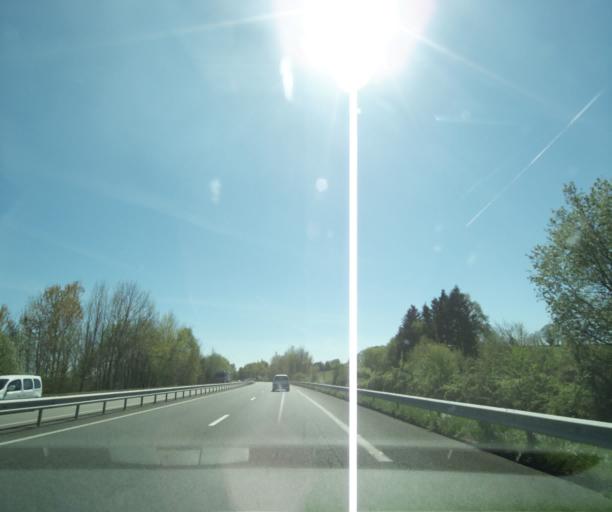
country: FR
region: Limousin
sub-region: Departement de la Correze
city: Uzerche
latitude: 45.4544
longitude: 1.5089
